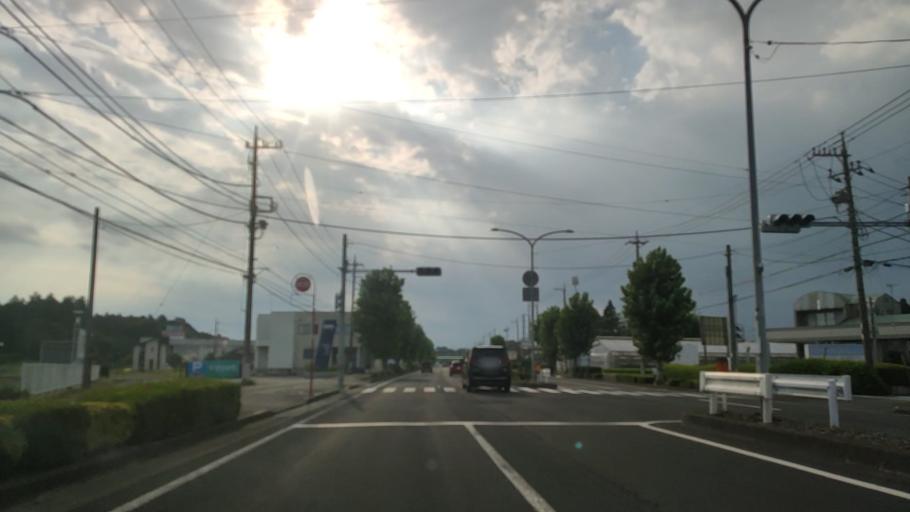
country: JP
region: Tochigi
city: Utsunomiya-shi
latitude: 36.5493
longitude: 139.8460
